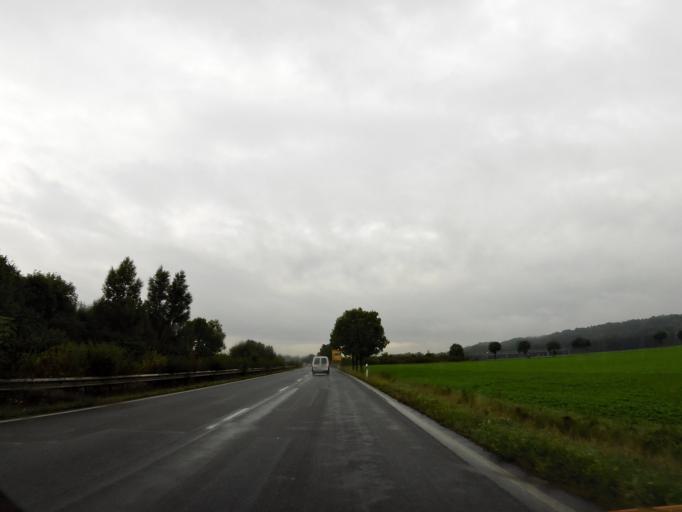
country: DE
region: Lower Saxony
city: Bovenden
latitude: 51.5647
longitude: 9.9196
